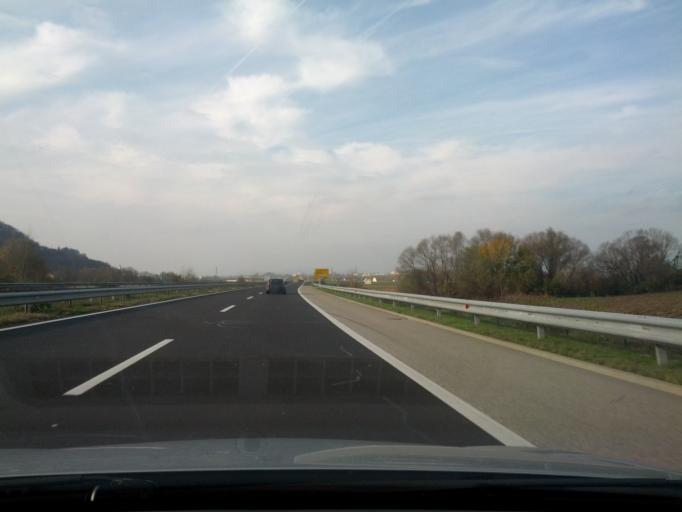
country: SI
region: Brezice
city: Brezice
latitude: 45.8818
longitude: 15.6226
